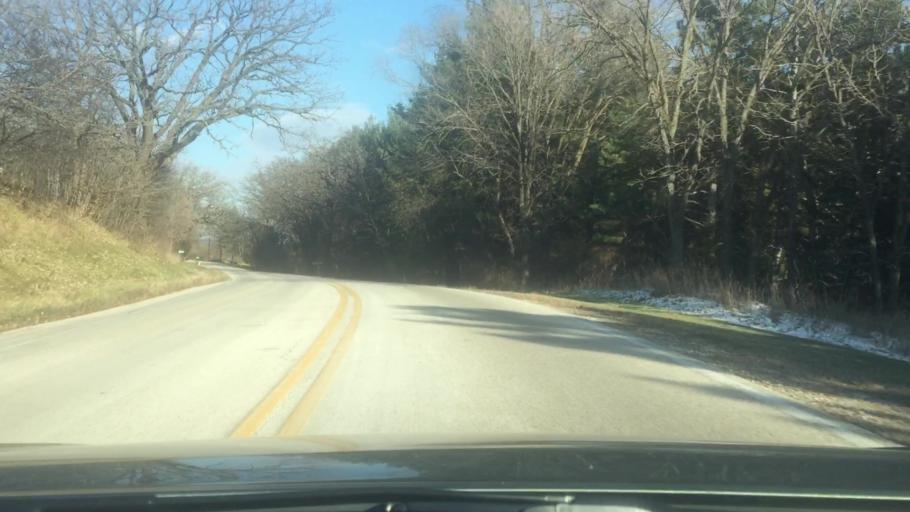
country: US
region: Wisconsin
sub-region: Waukesha County
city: Eagle
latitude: 42.9232
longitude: -88.5052
